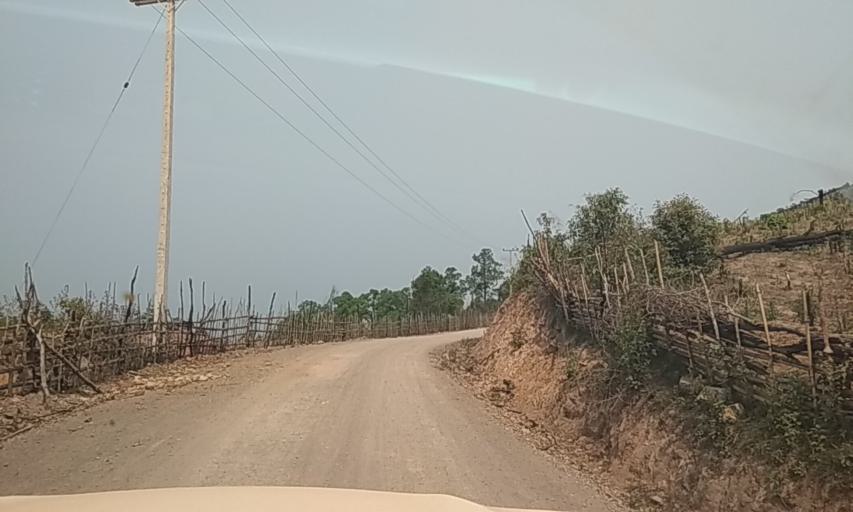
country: VN
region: Huyen Dien Bien
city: Dien Bien Phu
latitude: 21.4838
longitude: 102.7776
